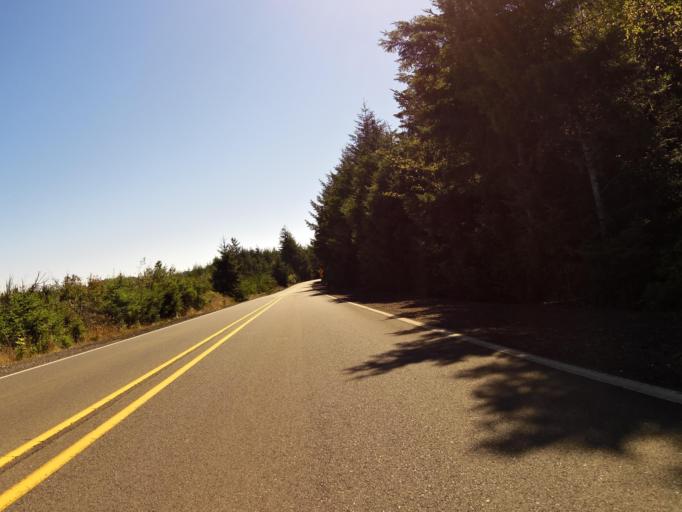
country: US
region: Oregon
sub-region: Coos County
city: Barview
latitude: 43.2447
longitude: -124.3332
